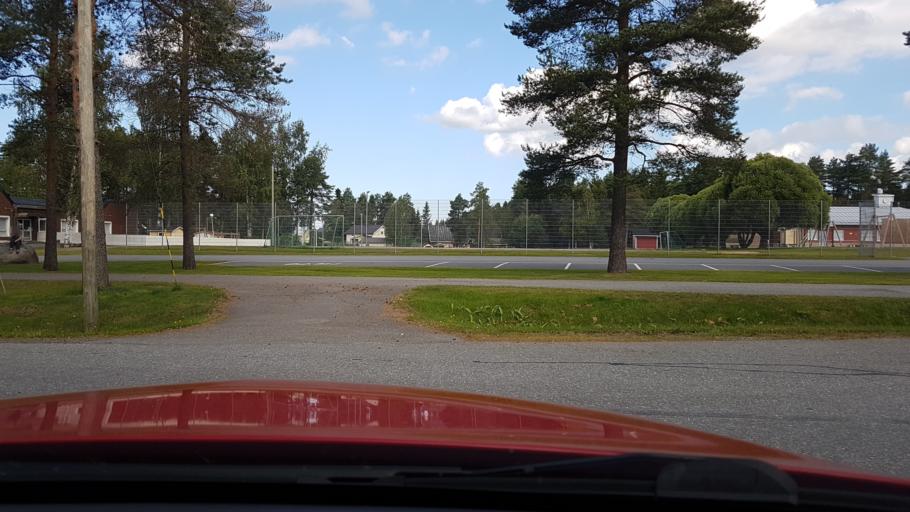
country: FI
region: Northern Ostrobothnia
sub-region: Ylivieska
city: Himanka
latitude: 64.0637
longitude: 23.6614
